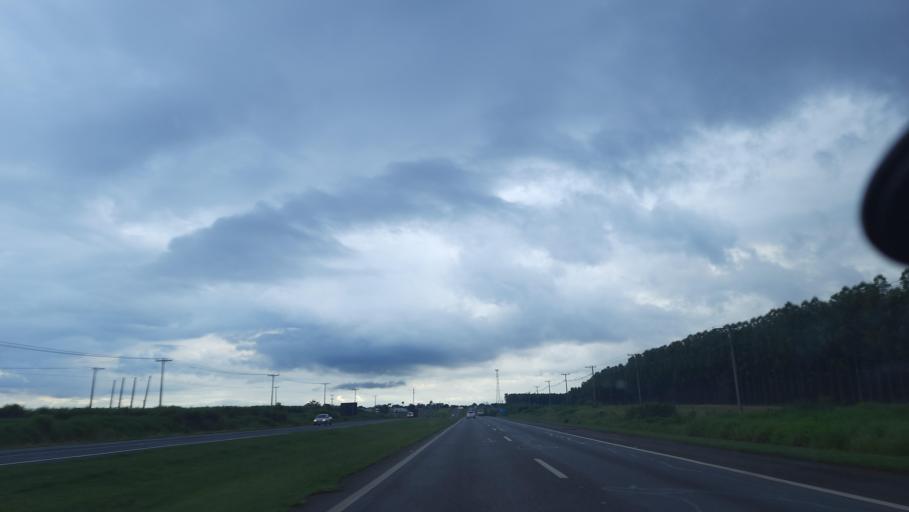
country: BR
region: Sao Paulo
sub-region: Moji-Guacu
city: Mogi-Gaucu
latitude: -22.3299
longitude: -46.9605
